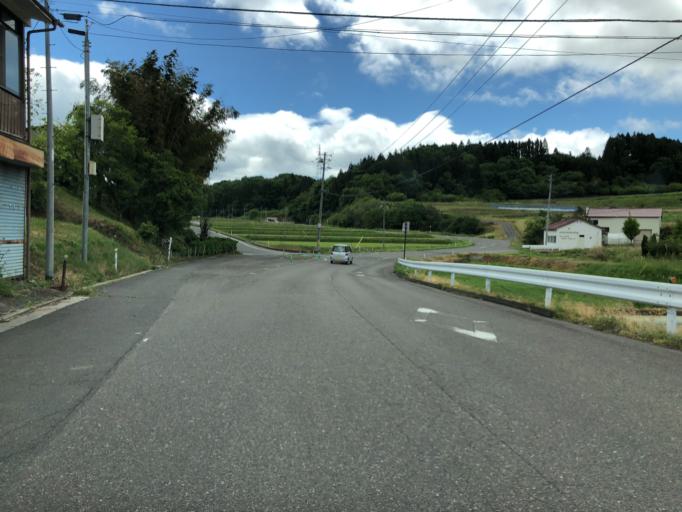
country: JP
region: Fukushima
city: Miharu
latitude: 37.4777
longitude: 140.4713
